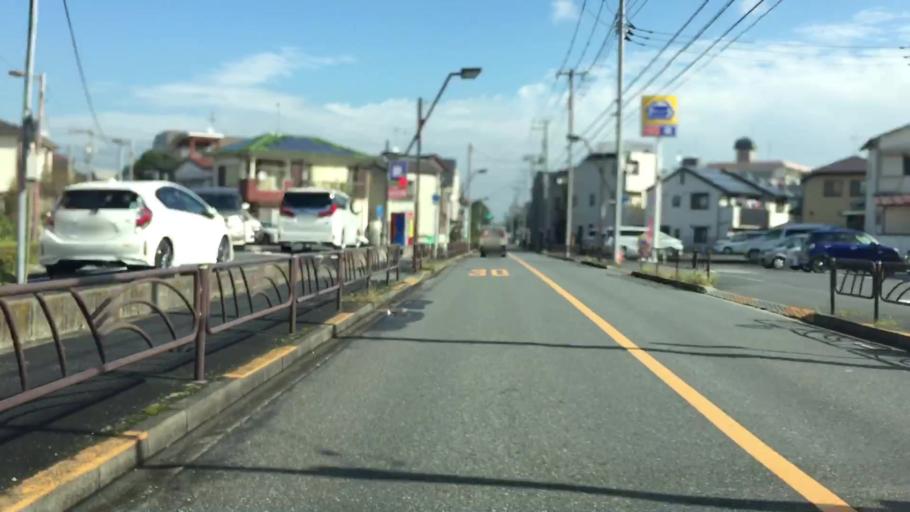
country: JP
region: Saitama
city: Yashio-shi
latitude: 35.7577
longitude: 139.8308
